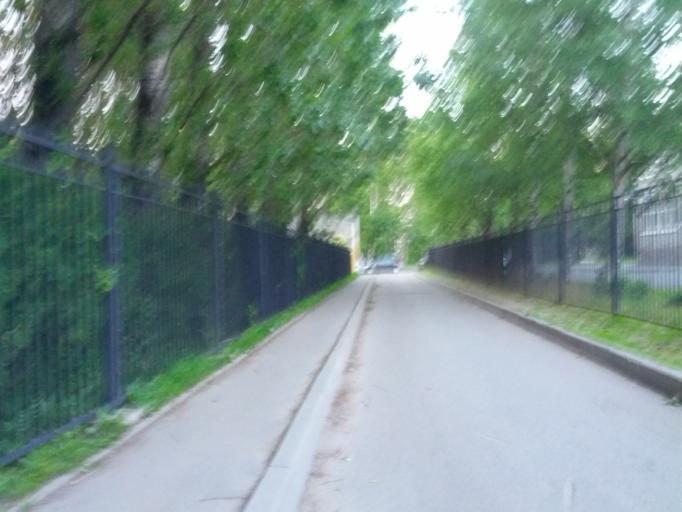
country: RU
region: St.-Petersburg
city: Obukhovo
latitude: 59.9058
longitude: 30.4715
